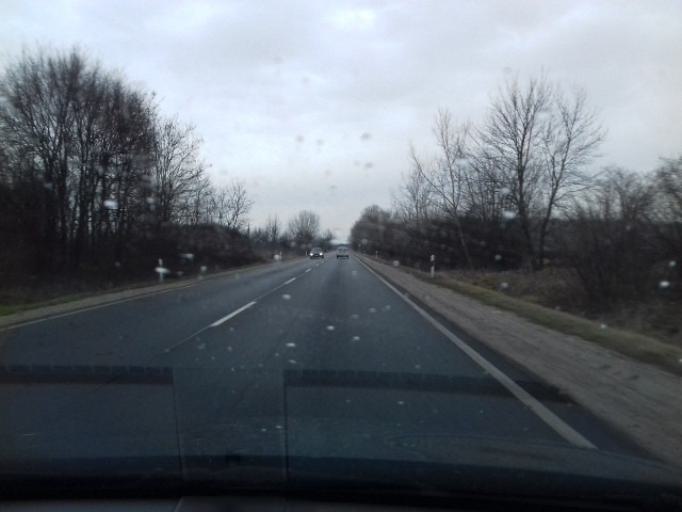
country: HU
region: Szabolcs-Szatmar-Bereg
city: Ujfeherto
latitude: 47.8457
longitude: 21.7044
